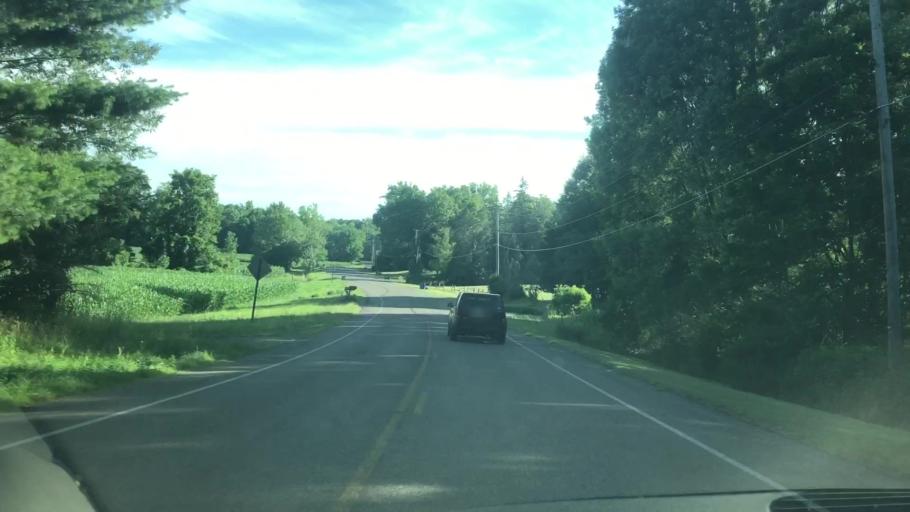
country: US
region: New York
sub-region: Wayne County
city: Macedon
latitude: 43.0482
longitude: -77.3379
